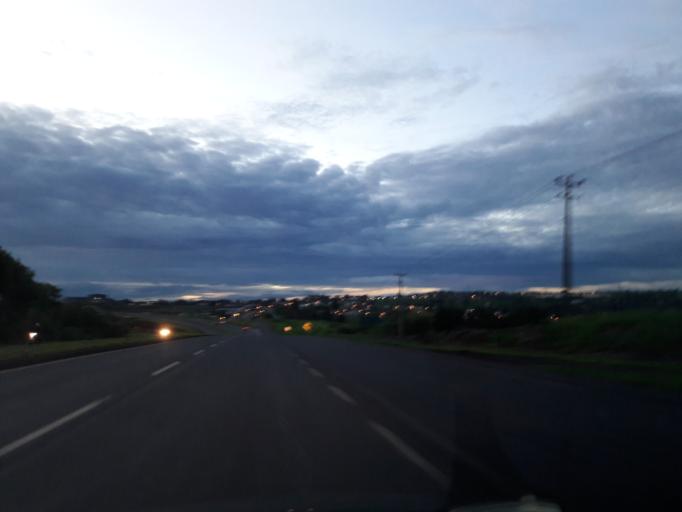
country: BR
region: Parana
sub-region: Marialva
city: Marialva
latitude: -23.4999
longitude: -51.7660
